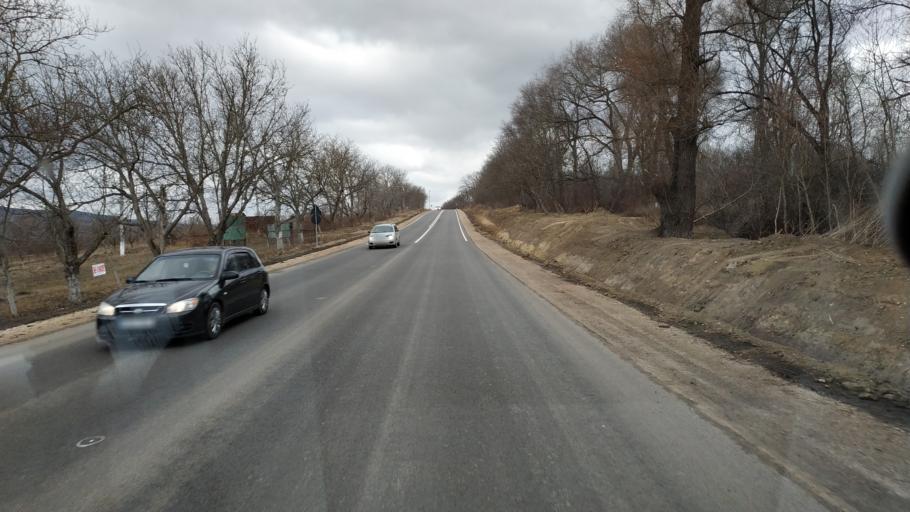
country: MD
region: Stinga Nistrului
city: Bucovat
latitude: 47.2189
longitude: 28.3993
